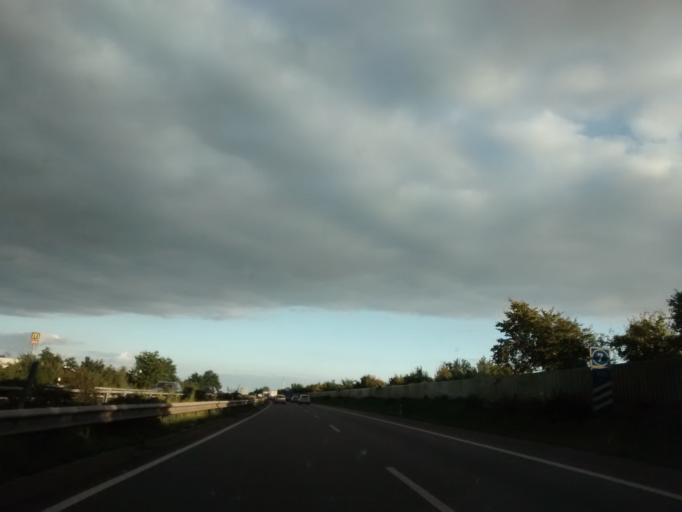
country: DE
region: North Rhine-Westphalia
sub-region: Regierungsbezirk Munster
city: Rheine
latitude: 52.3265
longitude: 7.4227
